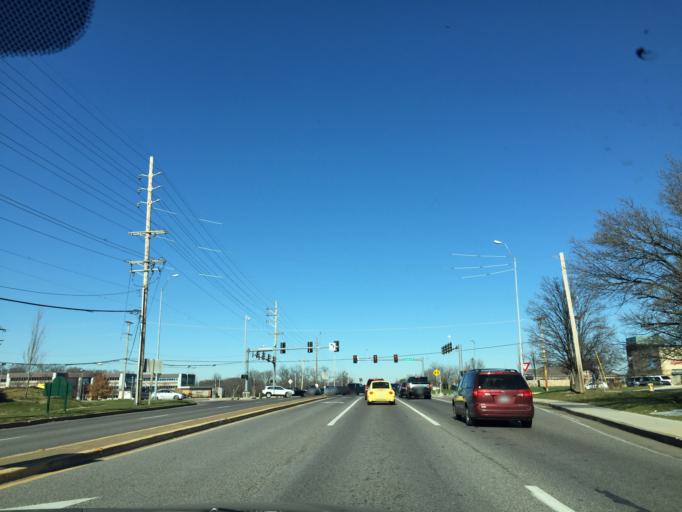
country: US
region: Missouri
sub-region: Saint Louis County
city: Ellisville
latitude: 38.6040
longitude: -90.5856
